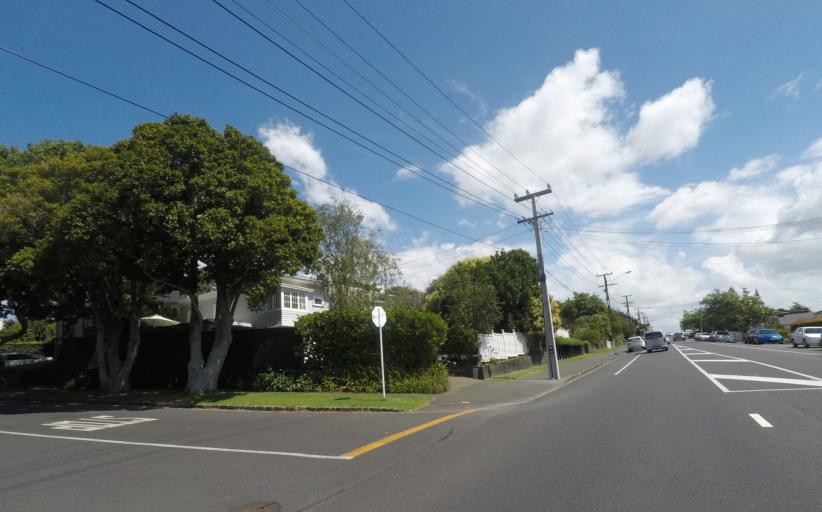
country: NZ
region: Auckland
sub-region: Auckland
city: Tamaki
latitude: -36.8919
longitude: 174.8123
